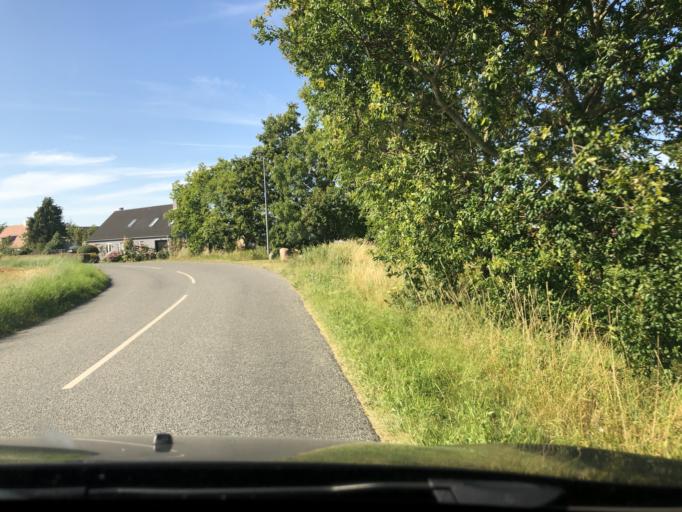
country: DK
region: South Denmark
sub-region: AEro Kommune
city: Marstal
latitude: 54.8651
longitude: 10.5031
